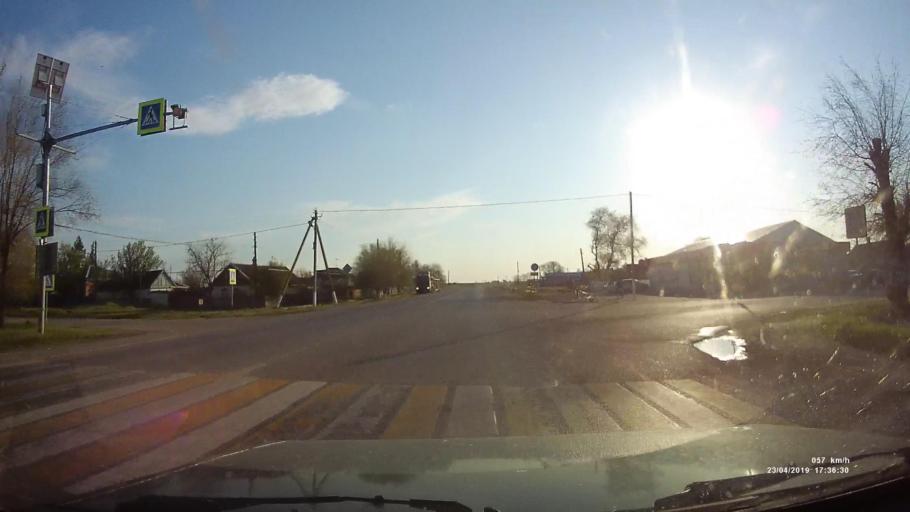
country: RU
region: Kalmykiya
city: Priyutnoye
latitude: 46.0961
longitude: 43.5057
